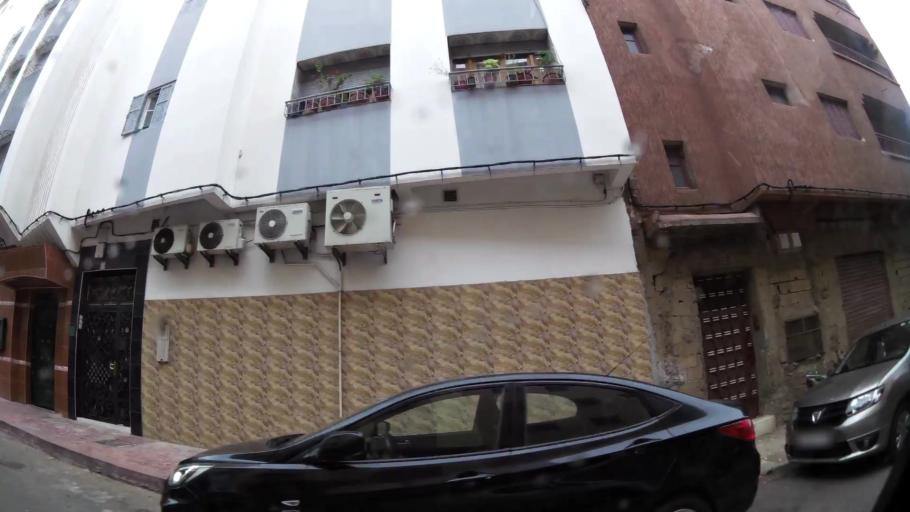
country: MA
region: Grand Casablanca
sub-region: Mediouna
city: Tit Mellil
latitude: 33.6090
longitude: -7.4959
